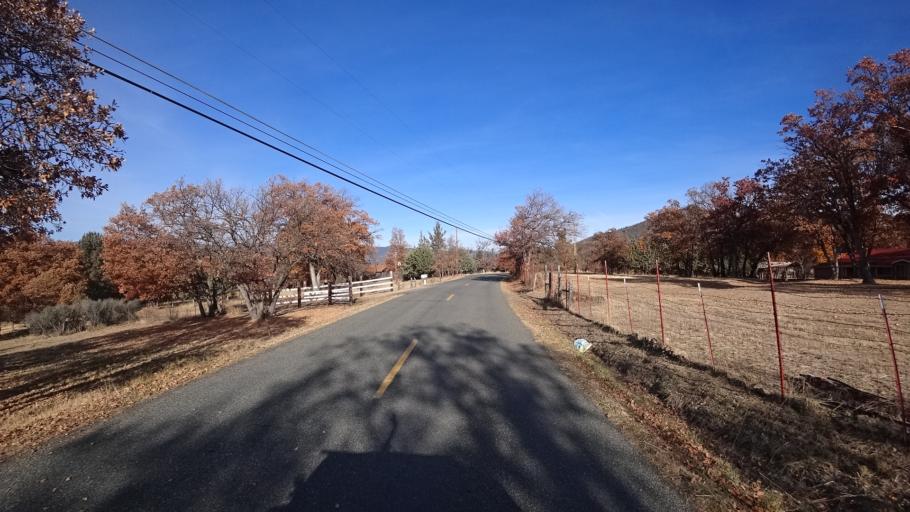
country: US
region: California
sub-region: Siskiyou County
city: Yreka
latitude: 41.6686
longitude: -122.6227
